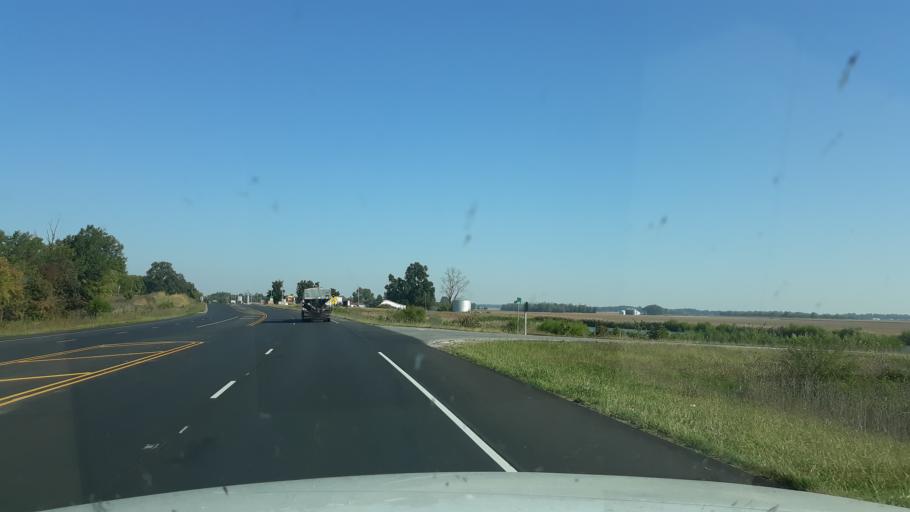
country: US
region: Illinois
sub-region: Saline County
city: Harrisburg
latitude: 37.7560
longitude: -88.5125
